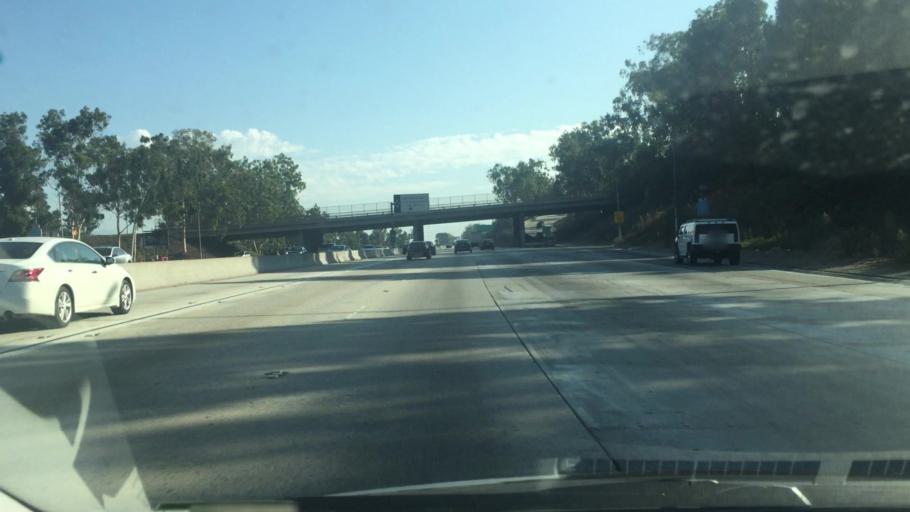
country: US
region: California
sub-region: Los Angeles County
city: West Whittier-Los Nietos
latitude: 34.0031
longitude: -118.0652
